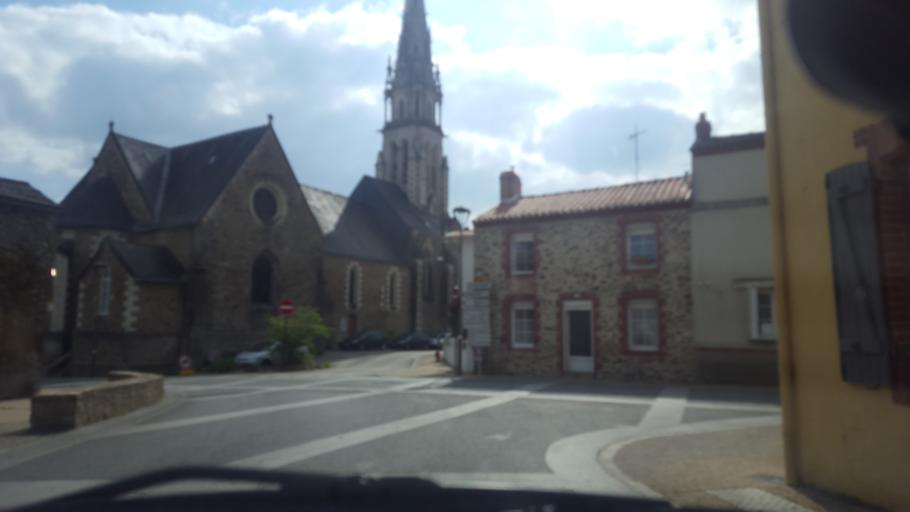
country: FR
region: Pays de la Loire
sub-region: Departement de la Loire-Atlantique
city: La Limouziniere
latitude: 46.9935
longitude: -1.5959
